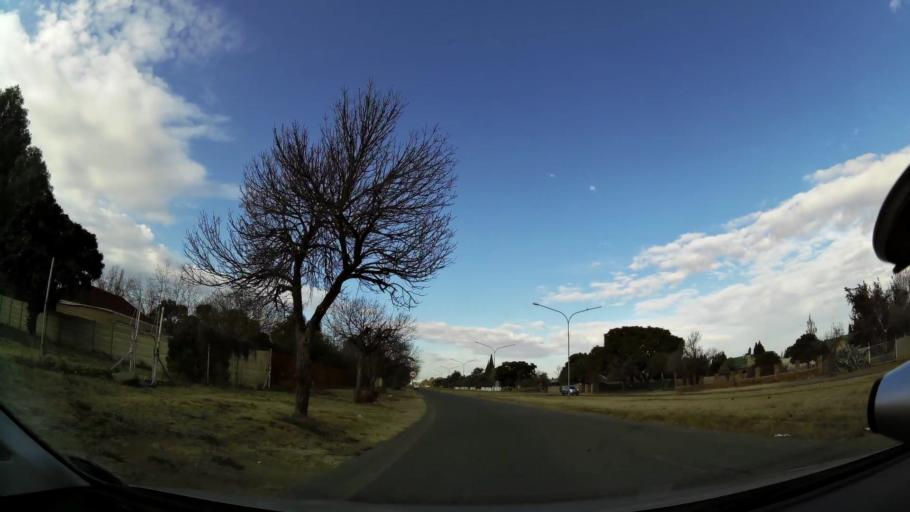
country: ZA
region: Orange Free State
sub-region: Lejweleputswa District Municipality
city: Welkom
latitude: -27.9892
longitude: 26.7147
